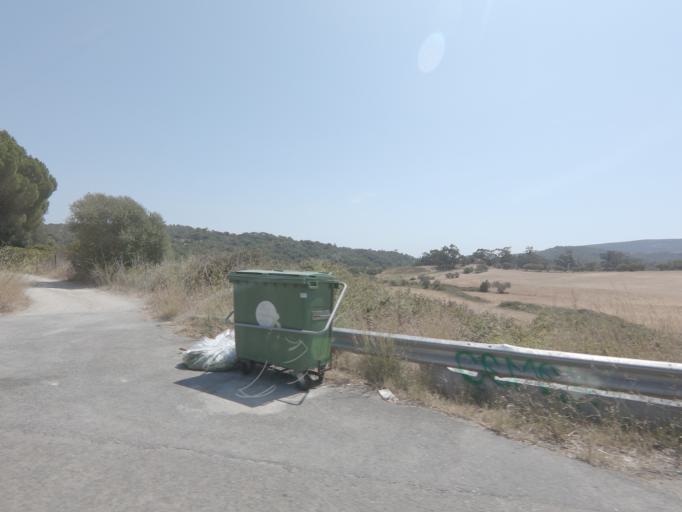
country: PT
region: Setubal
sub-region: Palmela
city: Quinta do Anjo
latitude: 38.5271
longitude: -8.9310
